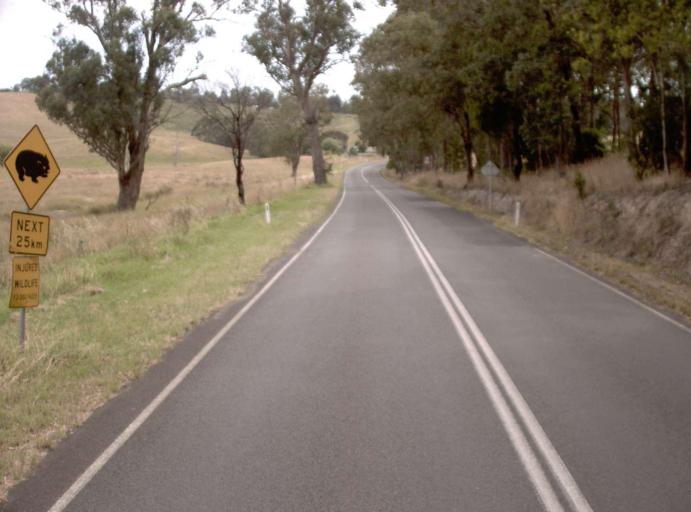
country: AU
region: Victoria
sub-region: Latrobe
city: Traralgon
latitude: -38.1455
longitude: 146.4793
